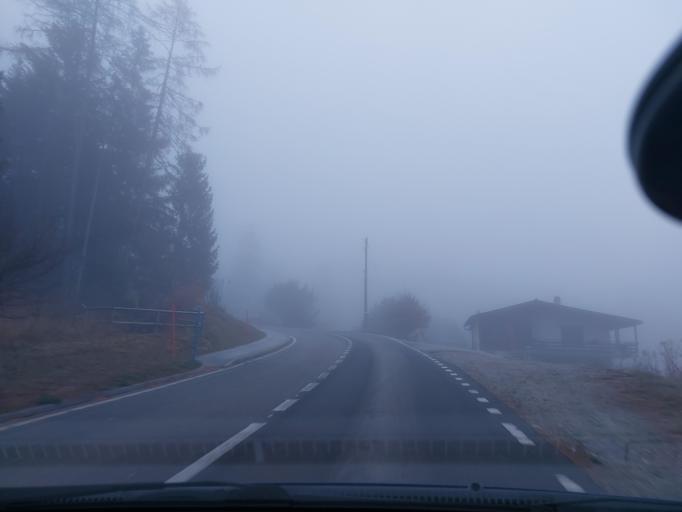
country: CH
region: Valais
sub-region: Sierre District
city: Lens
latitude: 46.2892
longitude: 7.4508
